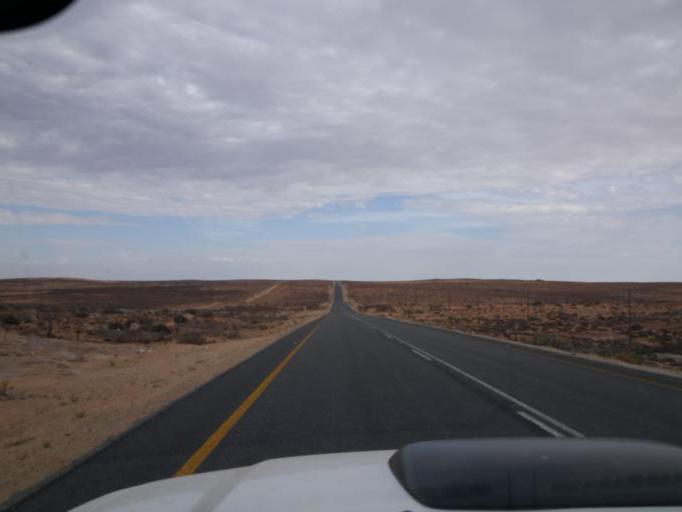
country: ZA
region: Northern Cape
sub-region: Namakwa District Municipality
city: Springbok
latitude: -29.4077
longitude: 17.8124
